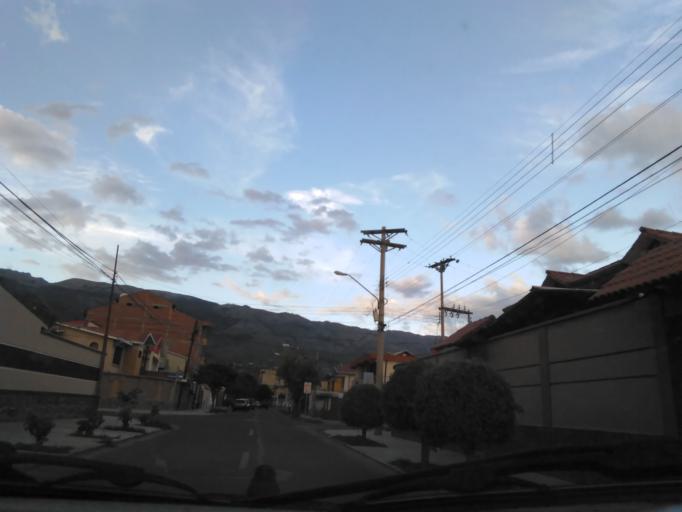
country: BO
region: Cochabamba
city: Cochabamba
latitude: -17.3841
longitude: -66.1659
